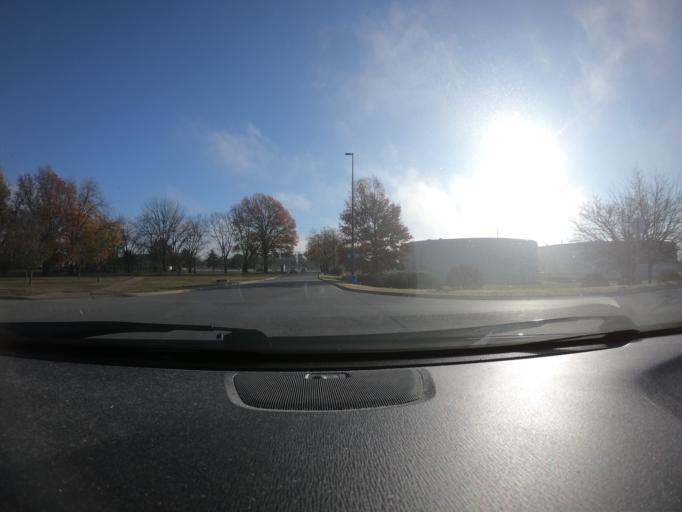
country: US
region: Arkansas
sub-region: Benton County
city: Bentonville
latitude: 36.3681
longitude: -94.2234
